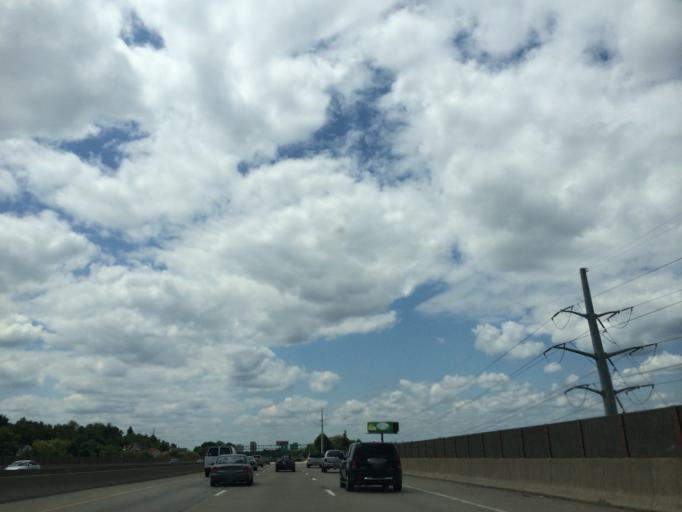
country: US
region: Pennsylvania
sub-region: Lackawanna County
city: Dunmore
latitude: 41.4086
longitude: -75.6256
